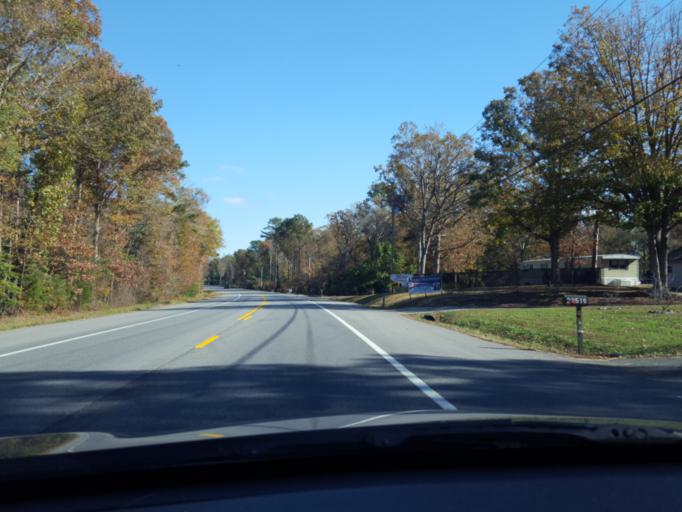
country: US
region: Maryland
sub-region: Saint Mary's County
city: Leonardtown
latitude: 38.2430
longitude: -76.5766
